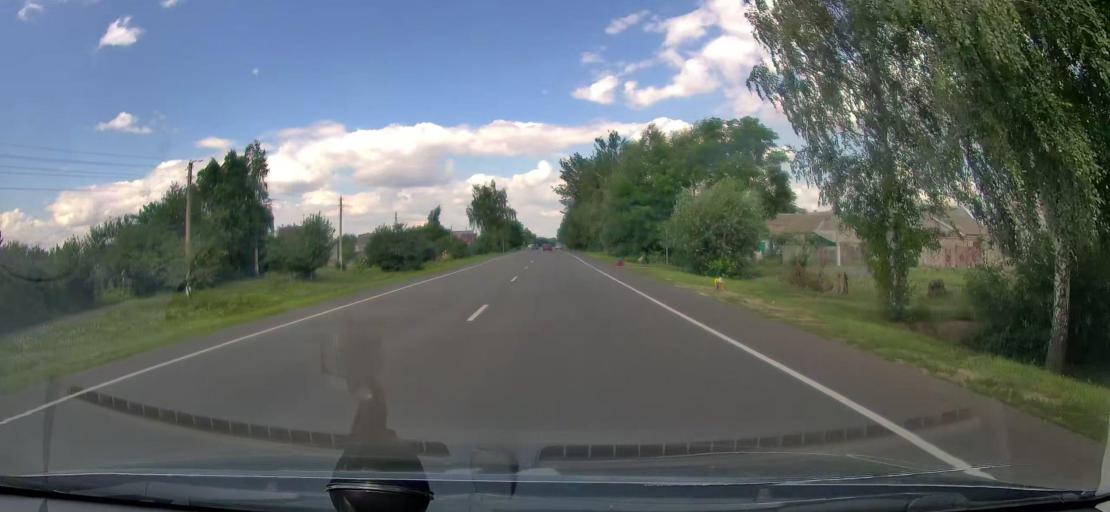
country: RU
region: Kursk
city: Zolotukhino
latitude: 51.9180
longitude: 36.3065
